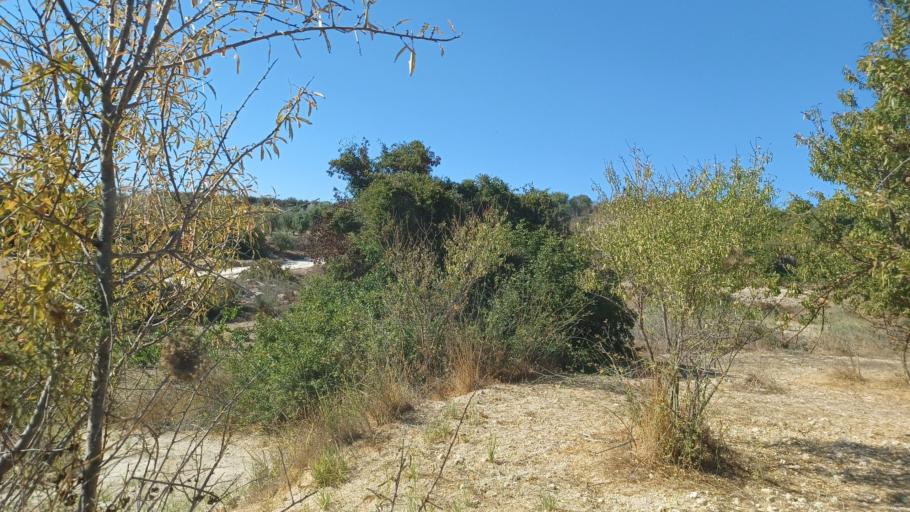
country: CY
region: Pafos
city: Mesogi
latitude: 34.8639
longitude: 32.5240
